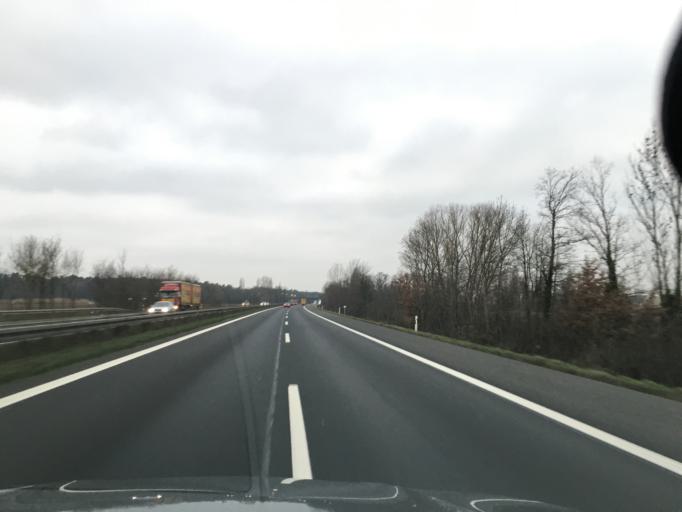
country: DE
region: Bavaria
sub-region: Regierungsbezirk Unterfranken
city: Kleinlangheim
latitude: 49.7810
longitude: 10.2589
